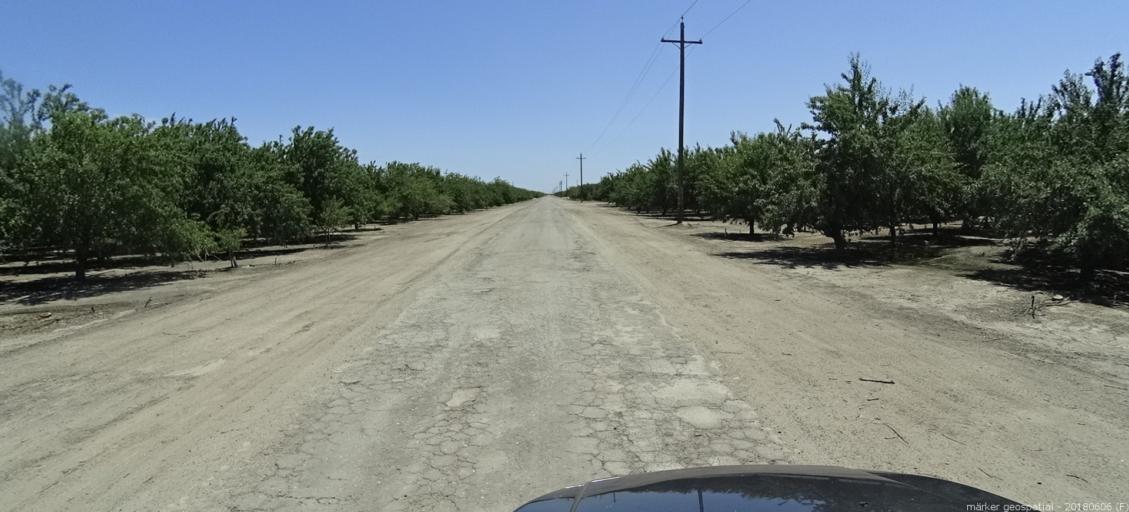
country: US
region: California
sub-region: Fresno County
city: Mendota
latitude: 36.8013
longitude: -120.3368
